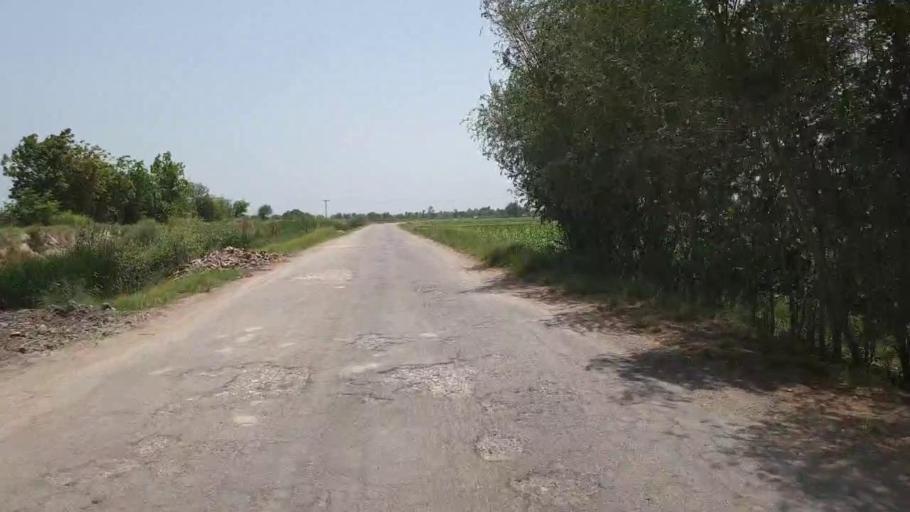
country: PK
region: Sindh
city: Daur
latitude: 26.3831
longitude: 68.1773
